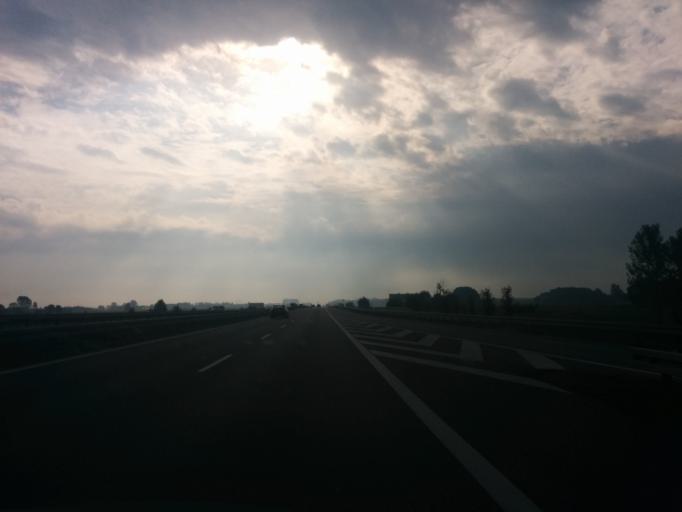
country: PL
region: Masovian Voivodeship
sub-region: Powiat radomski
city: Jedlinsk
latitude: 51.5417
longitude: 21.0614
